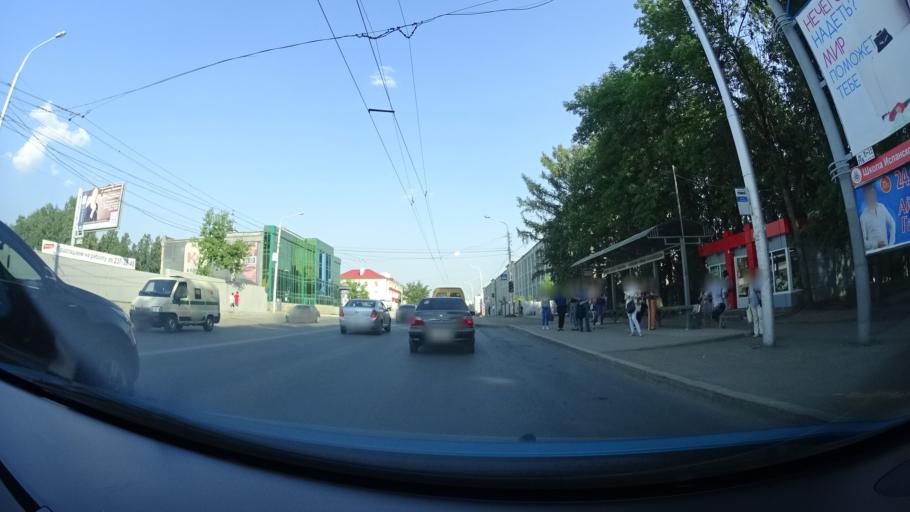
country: RU
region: Bashkortostan
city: Ufa
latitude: 54.7534
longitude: 56.0104
